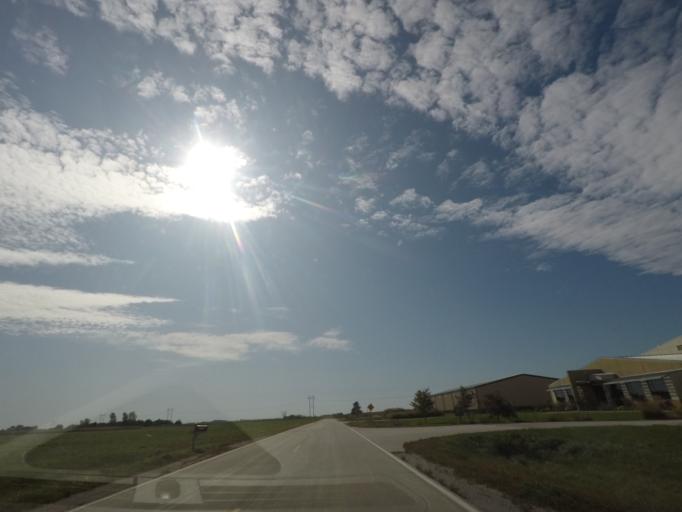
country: US
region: Iowa
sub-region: Boone County
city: Boone
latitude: 42.0201
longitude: -93.7768
